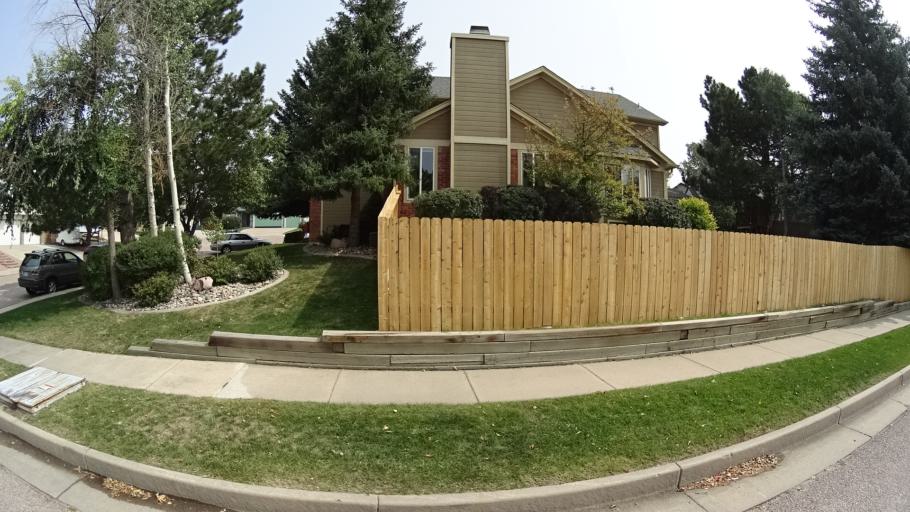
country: US
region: Colorado
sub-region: El Paso County
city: Cimarron Hills
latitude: 38.9171
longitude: -104.7413
